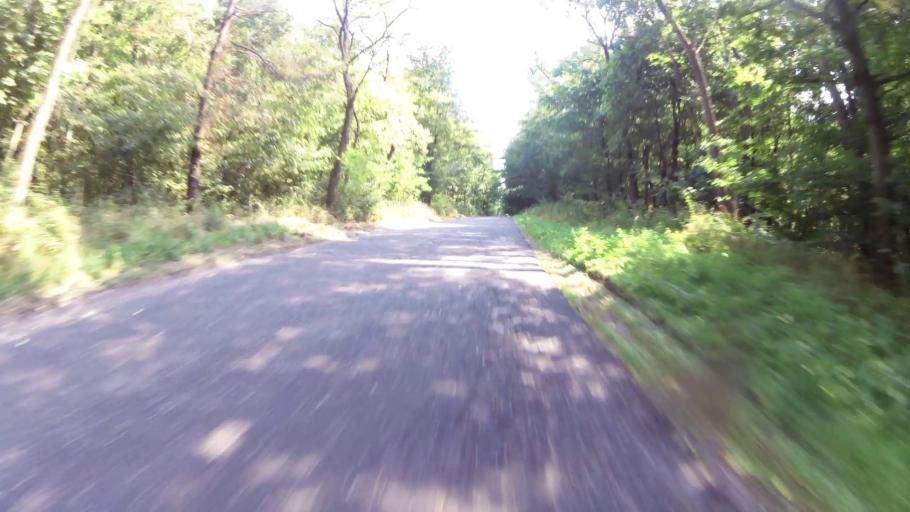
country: PL
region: West Pomeranian Voivodeship
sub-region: Powiat mysliborski
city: Debno
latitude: 52.8525
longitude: 14.6981
